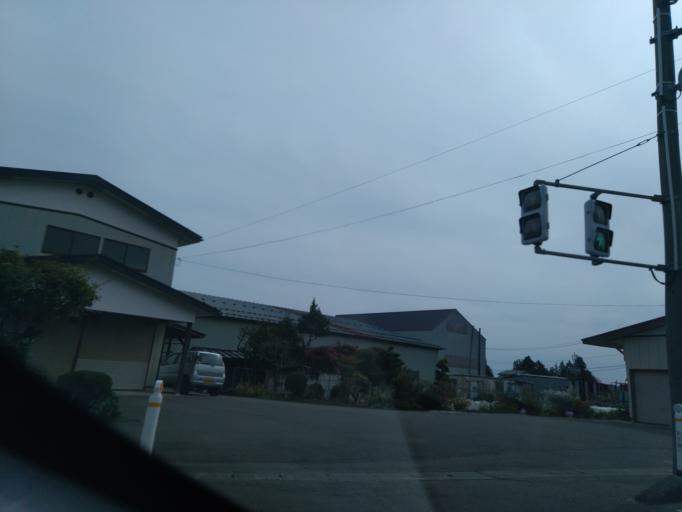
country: JP
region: Iwate
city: Hanamaki
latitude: 39.4444
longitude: 141.0856
